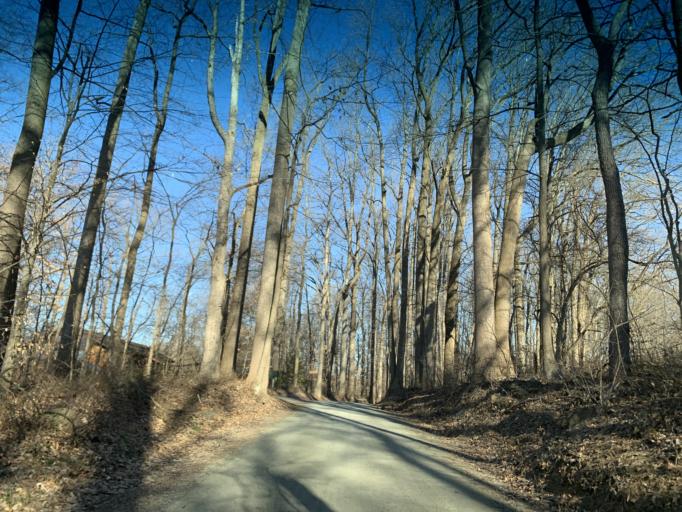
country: US
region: Maryland
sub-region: Harford County
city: Aberdeen
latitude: 39.6128
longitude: -76.2366
